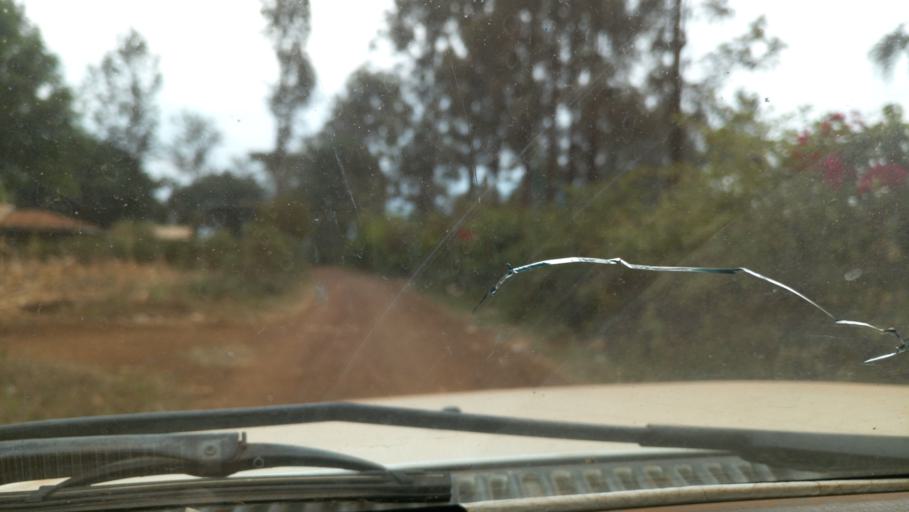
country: KE
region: Murang'a District
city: Maragua
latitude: -0.8790
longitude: 37.1901
